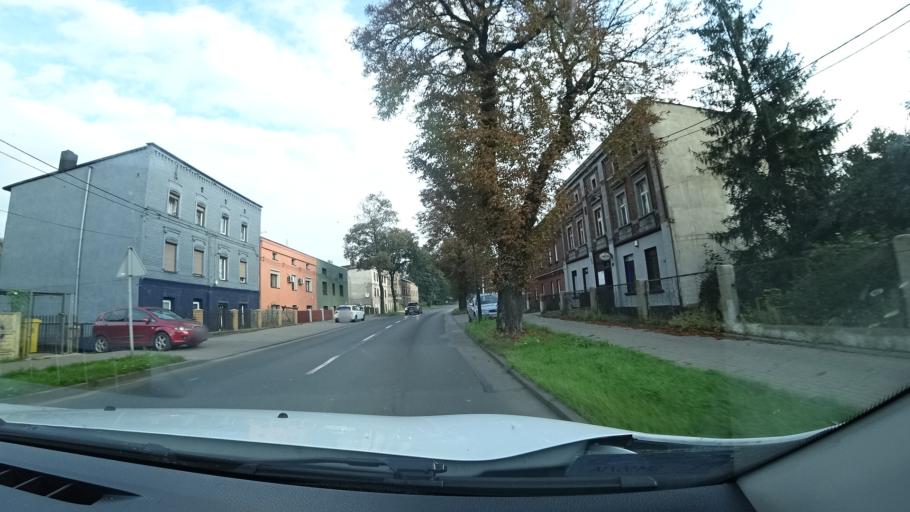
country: PL
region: Silesian Voivodeship
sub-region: Piekary Slaskie
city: Brzeziny Slaskie
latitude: 50.3492
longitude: 18.9809
